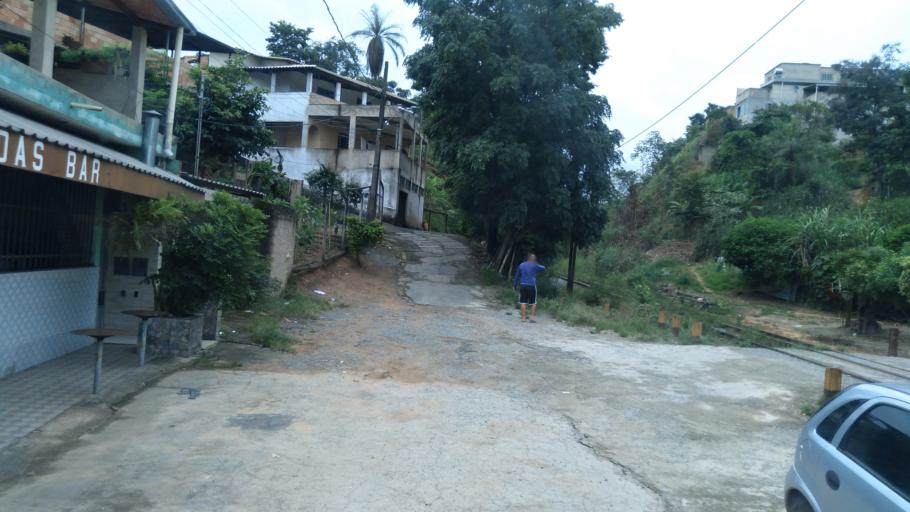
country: BR
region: Minas Gerais
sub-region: Santa Luzia
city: Santa Luzia
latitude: -19.8367
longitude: -43.8664
